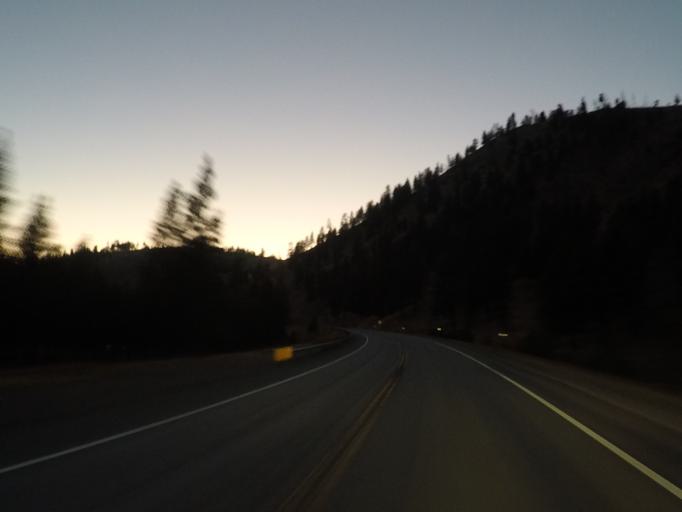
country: US
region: Montana
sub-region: Missoula County
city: Seeley Lake
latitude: 47.0250
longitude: -113.3072
